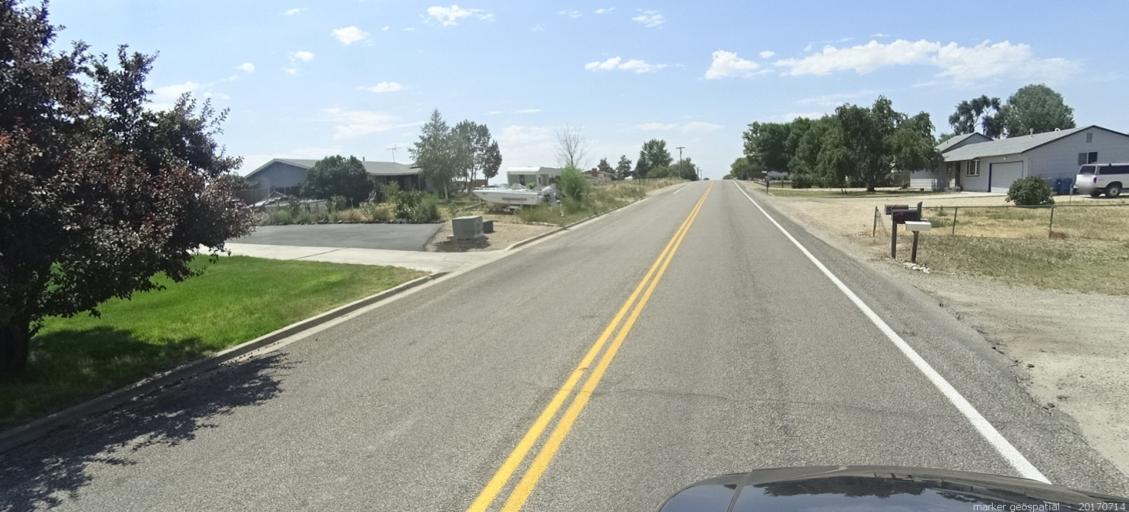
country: US
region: Idaho
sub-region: Ada County
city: Meridian
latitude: 43.5320
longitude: -116.3163
